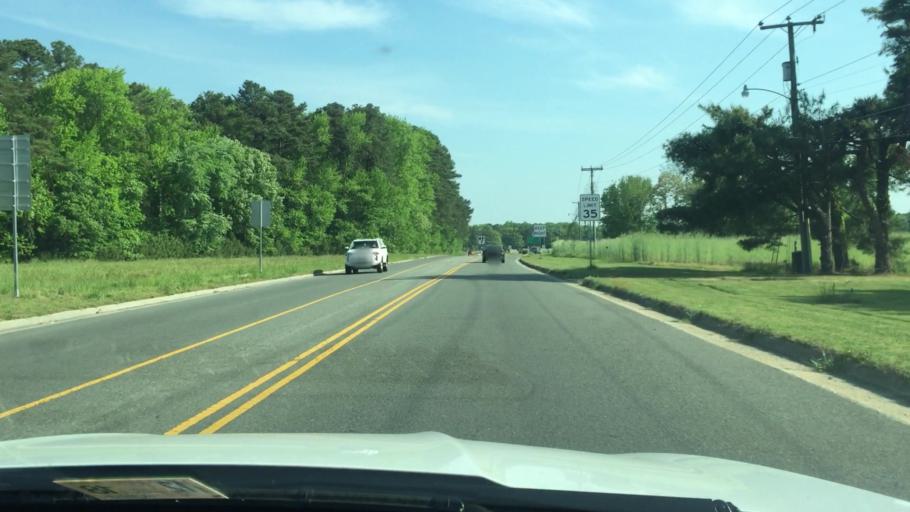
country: US
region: Virginia
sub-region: Lancaster County
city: Kilmarnock
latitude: 37.6515
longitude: -76.3887
